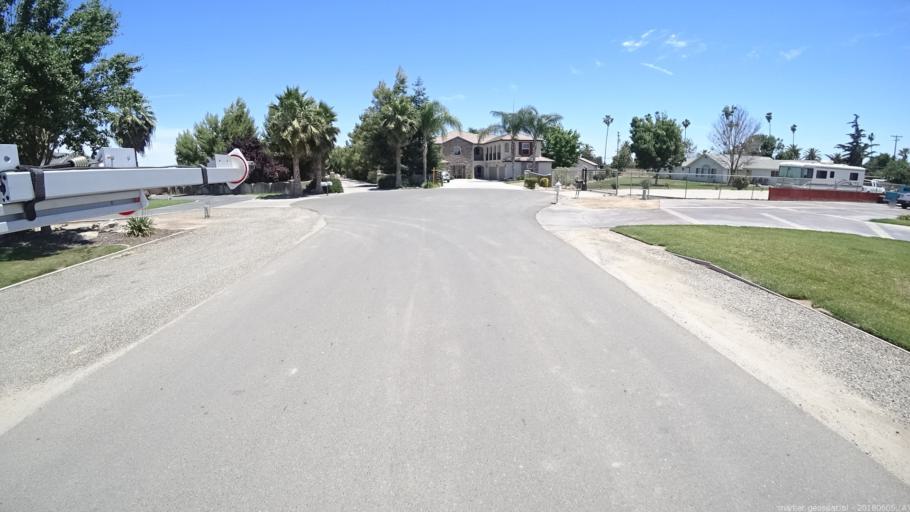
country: US
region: California
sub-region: Madera County
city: Chowchilla
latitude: 37.0934
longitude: -120.2913
